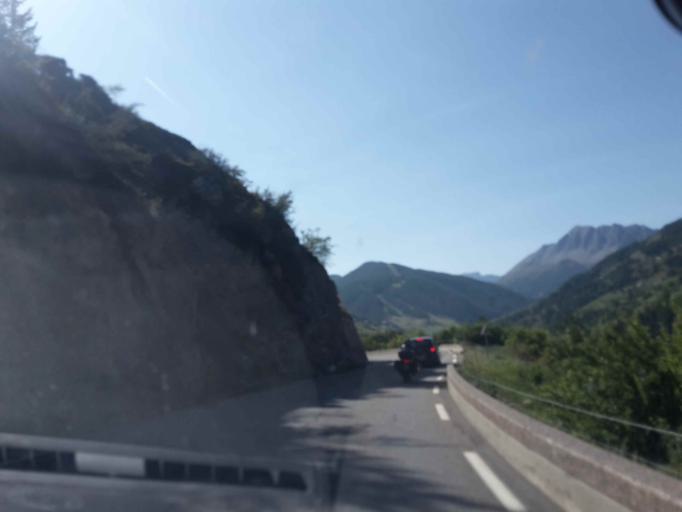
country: FR
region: Provence-Alpes-Cote d'Azur
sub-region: Departement des Hautes-Alpes
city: Guillestre
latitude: 44.6168
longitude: 6.6852
